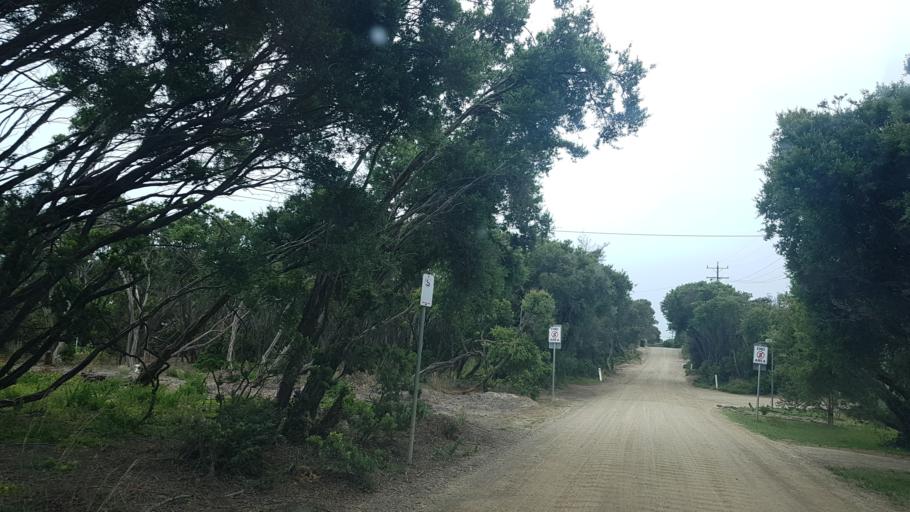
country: AU
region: Victoria
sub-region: Mornington Peninsula
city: Blairgowrie
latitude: -38.3705
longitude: 144.7690
